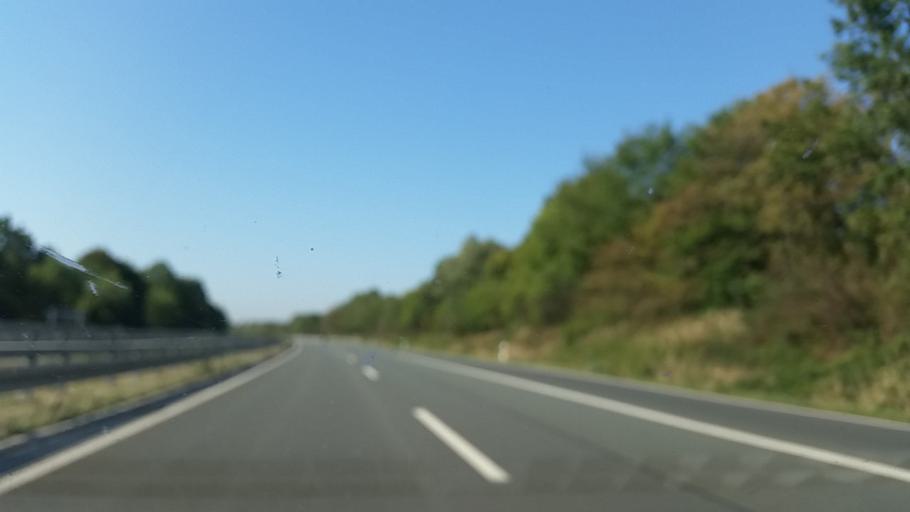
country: DE
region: North Rhine-Westphalia
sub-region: Regierungsbezirk Dusseldorf
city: Langenfeld
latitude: 51.1093
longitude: 6.9751
